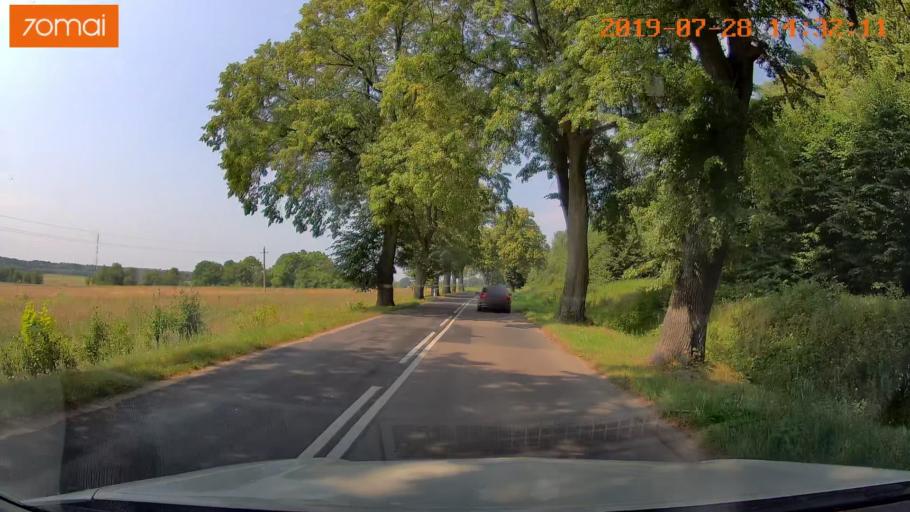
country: RU
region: Kaliningrad
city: Primorsk
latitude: 54.8111
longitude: 20.0440
